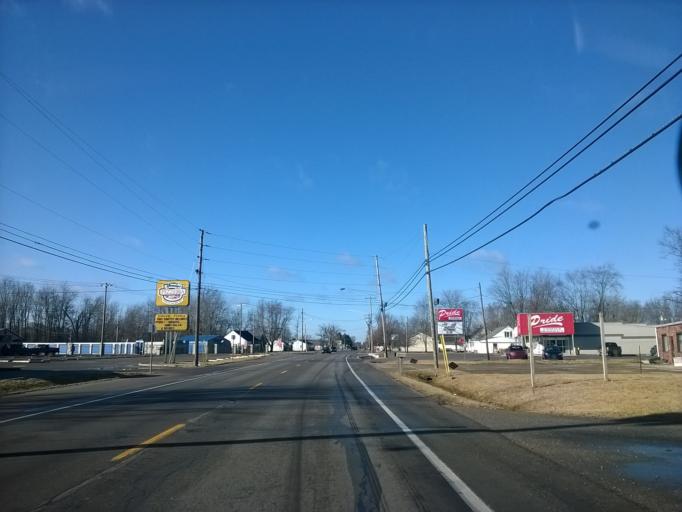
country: US
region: Indiana
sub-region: Jefferson County
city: Hanover
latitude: 38.7150
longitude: -85.4774
